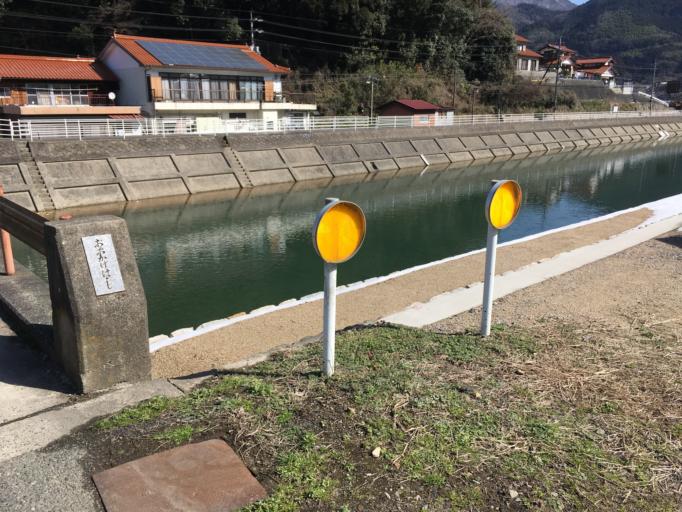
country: JP
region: Shimane
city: Masuda
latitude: 34.4521
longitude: 131.7583
